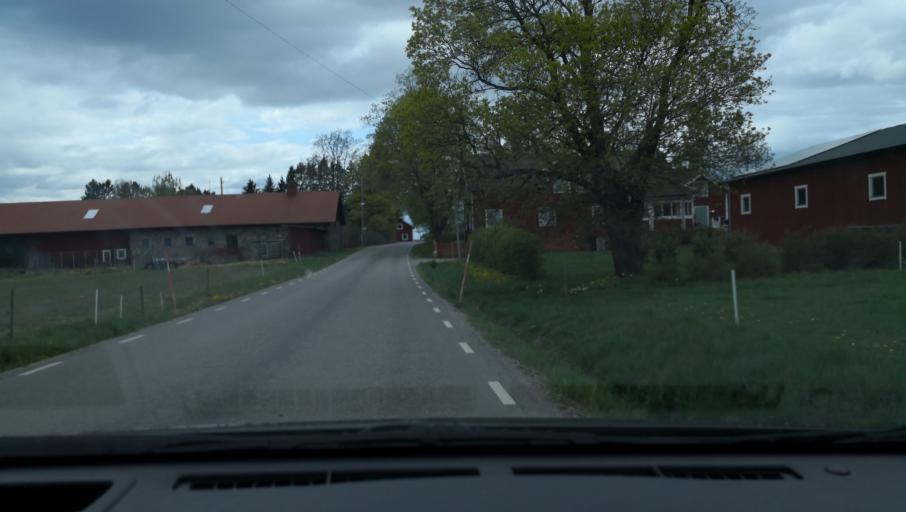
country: SE
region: Dalarna
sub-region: Avesta Kommun
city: Avesta
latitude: 60.0223
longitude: 16.3086
